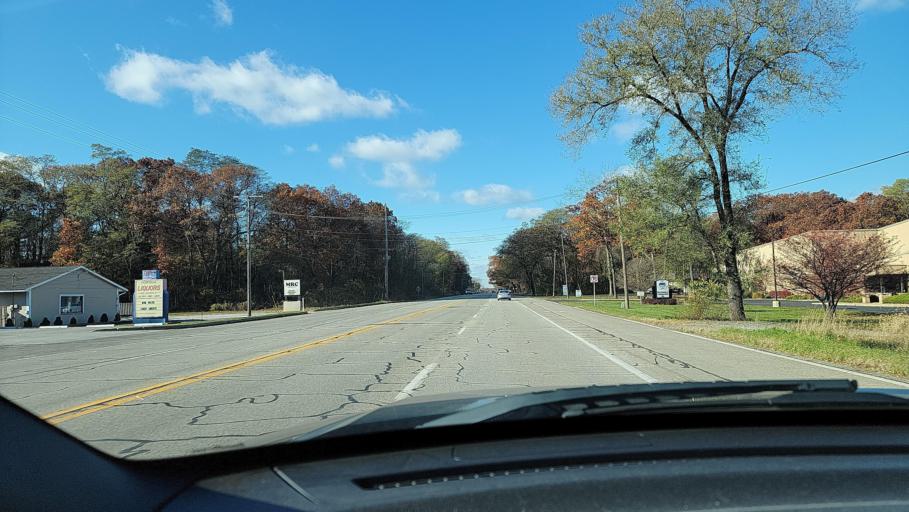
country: US
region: Indiana
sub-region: Porter County
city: Portage
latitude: 41.5989
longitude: -87.1575
